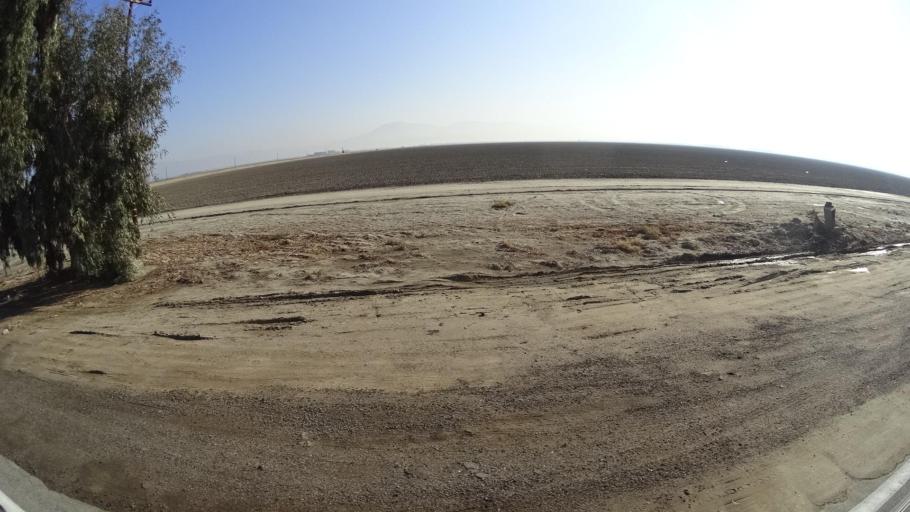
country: US
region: California
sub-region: Kern County
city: Greenfield
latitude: 35.1778
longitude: -119.0032
